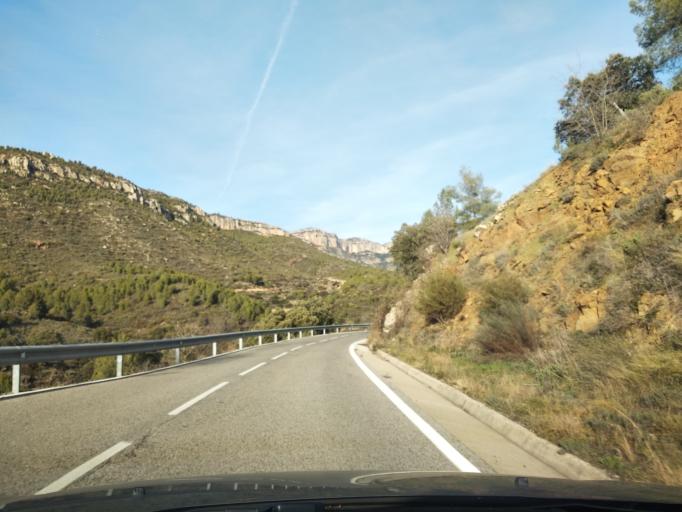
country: ES
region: Catalonia
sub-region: Provincia de Tarragona
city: la Morera de Montsant
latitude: 41.2423
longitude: 0.7903
